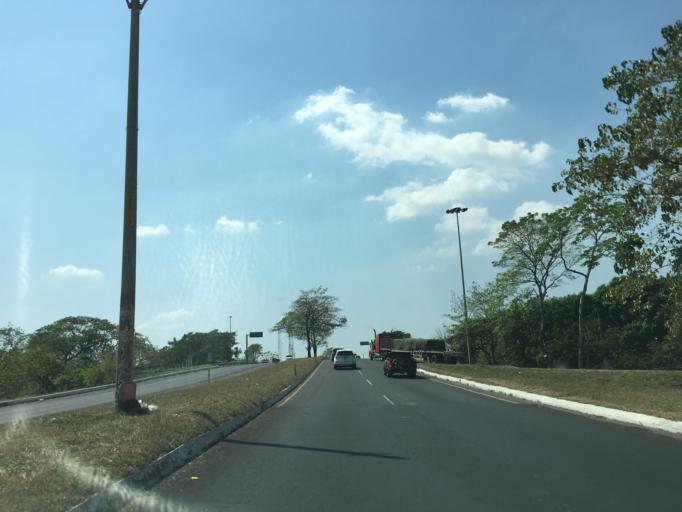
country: GT
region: Escuintla
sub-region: Municipio de Escuintla
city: Escuintla
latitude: 14.2902
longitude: -90.7974
